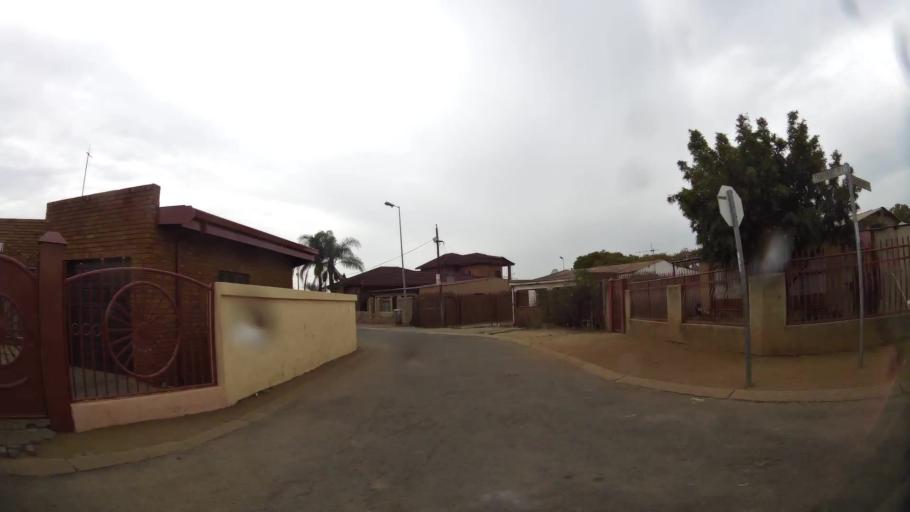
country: ZA
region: Gauteng
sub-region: City of Tshwane Metropolitan Municipality
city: Pretoria
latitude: -25.7143
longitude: 28.3538
